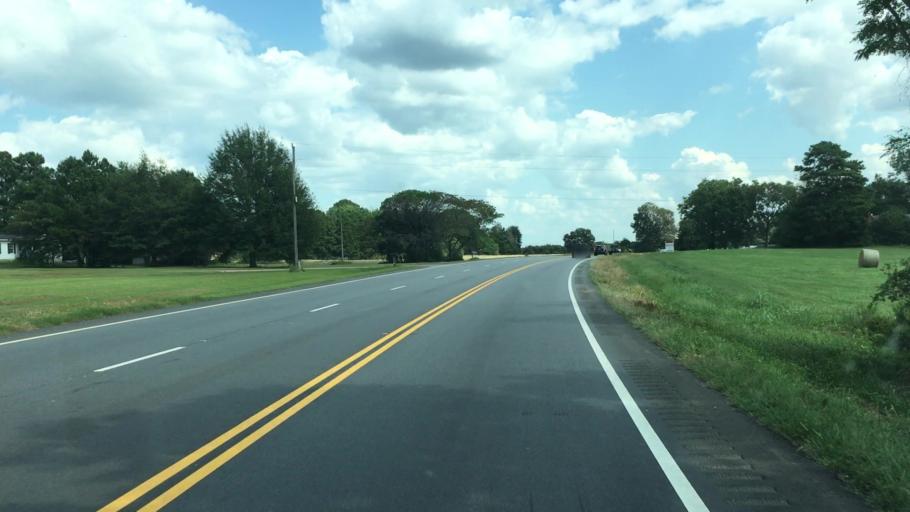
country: US
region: Georgia
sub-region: Putnam County
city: Jefferson
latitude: 33.4711
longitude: -83.4196
